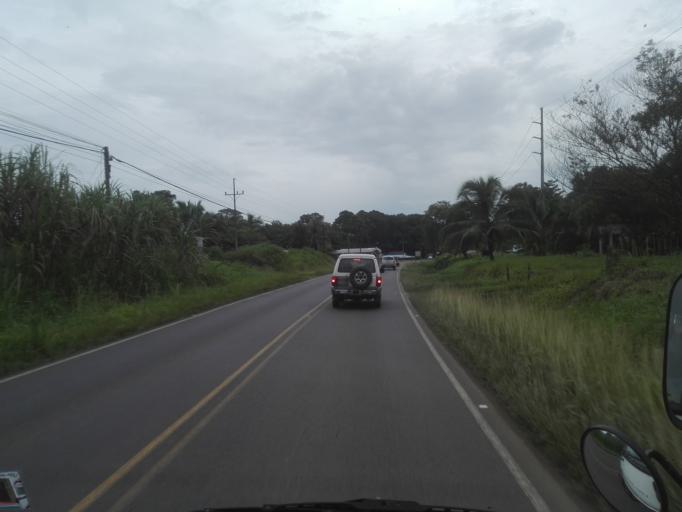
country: CR
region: Heredia
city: La Virgen
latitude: 10.3963
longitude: -83.9677
